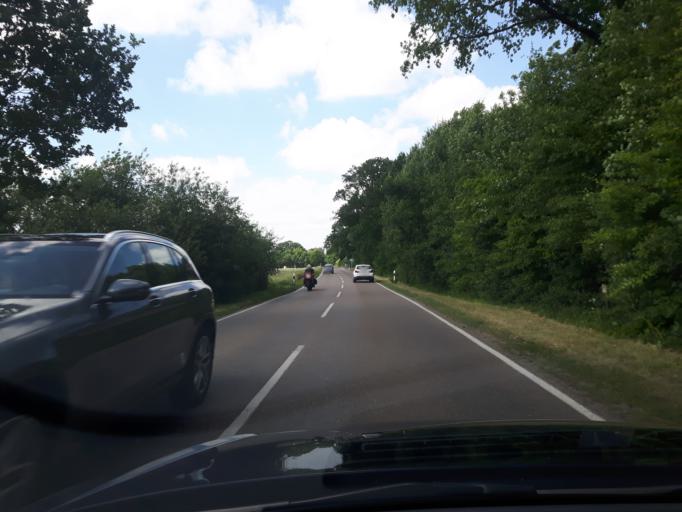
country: DE
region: Schleswig-Holstein
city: Sierksdorf
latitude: 54.0783
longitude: 10.7771
